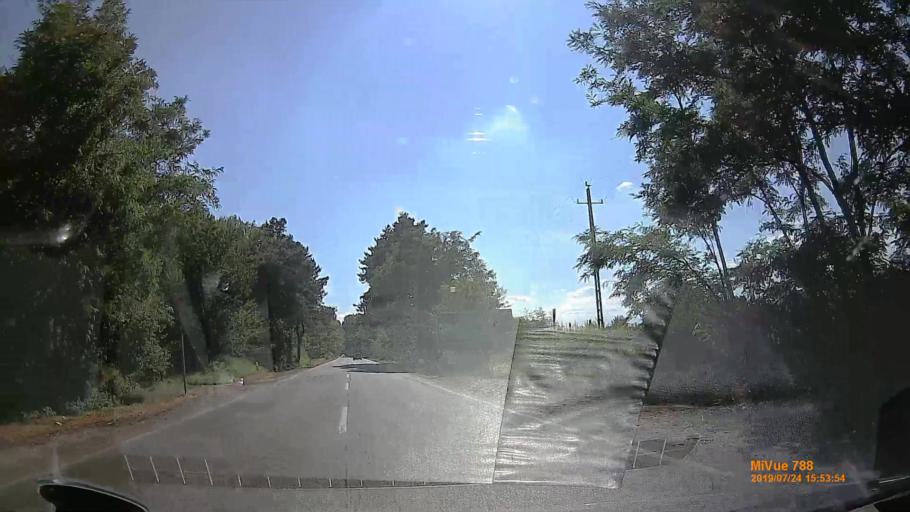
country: HU
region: Szabolcs-Szatmar-Bereg
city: Vaja
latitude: 48.0173
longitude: 22.1425
